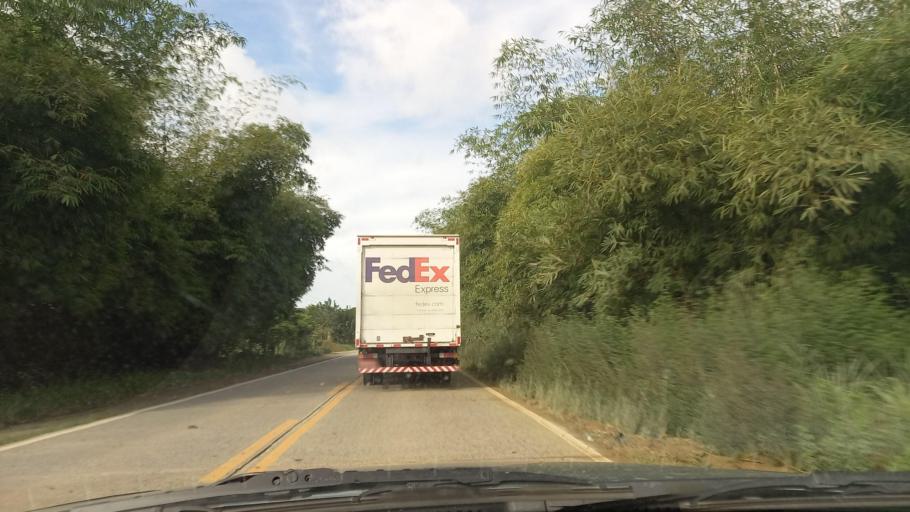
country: BR
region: Pernambuco
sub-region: Catende
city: Catende
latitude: -8.6928
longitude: -35.6805
